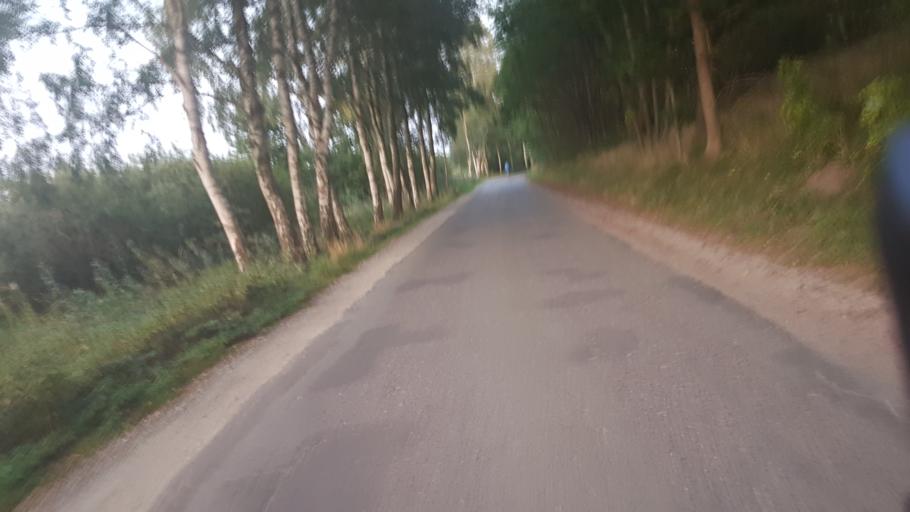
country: DE
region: Mecklenburg-Vorpommern
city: Ostseebad Binz
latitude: 54.3635
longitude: 13.6228
